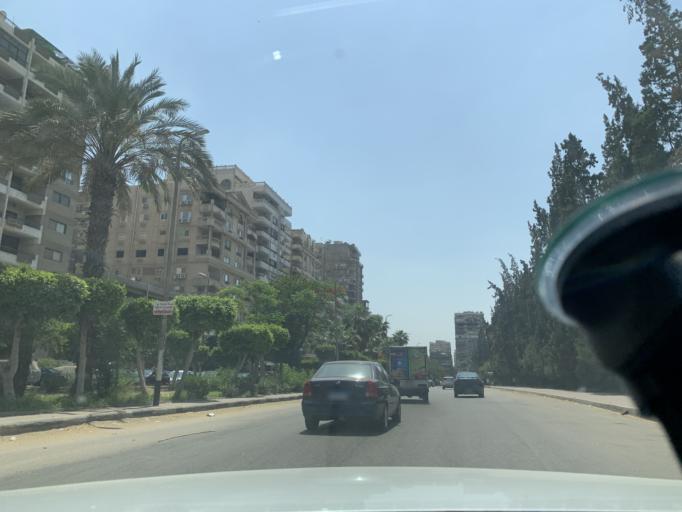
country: EG
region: Muhafazat al Qahirah
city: Cairo
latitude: 30.0609
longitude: 31.3495
